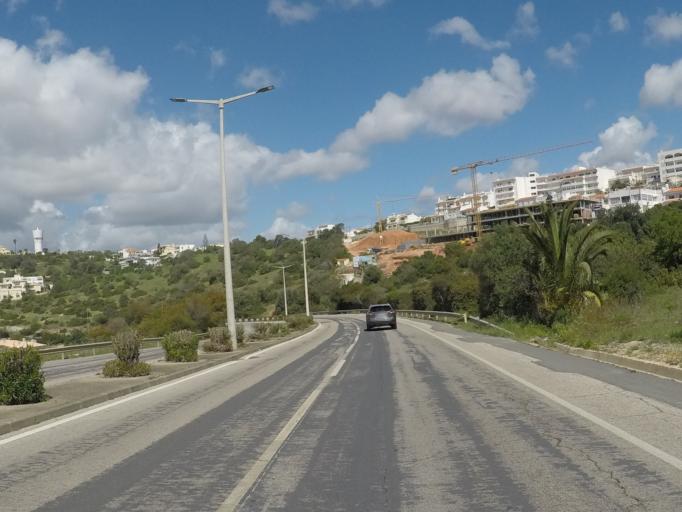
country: PT
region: Faro
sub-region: Albufeira
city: Albufeira
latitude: 37.0908
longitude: -8.2634
